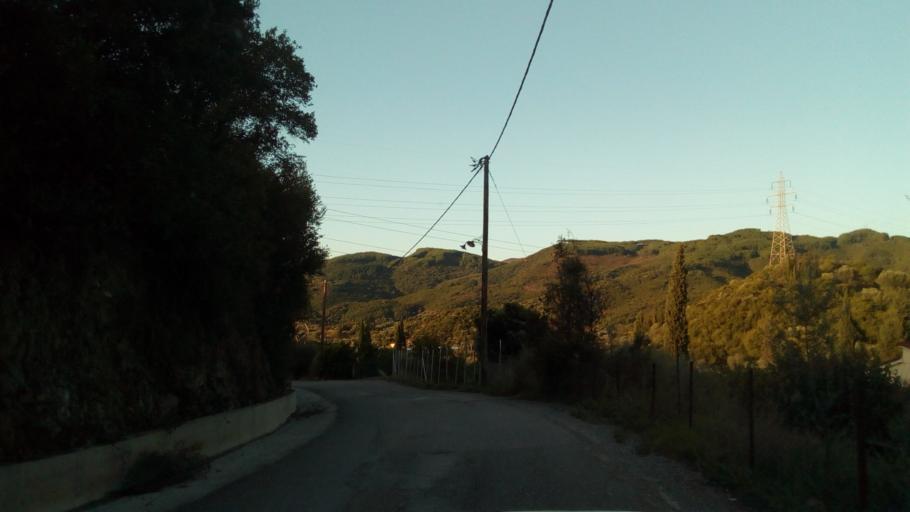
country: GR
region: West Greece
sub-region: Nomos Aitolias kai Akarnanias
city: Nafpaktos
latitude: 38.4046
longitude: 21.7969
